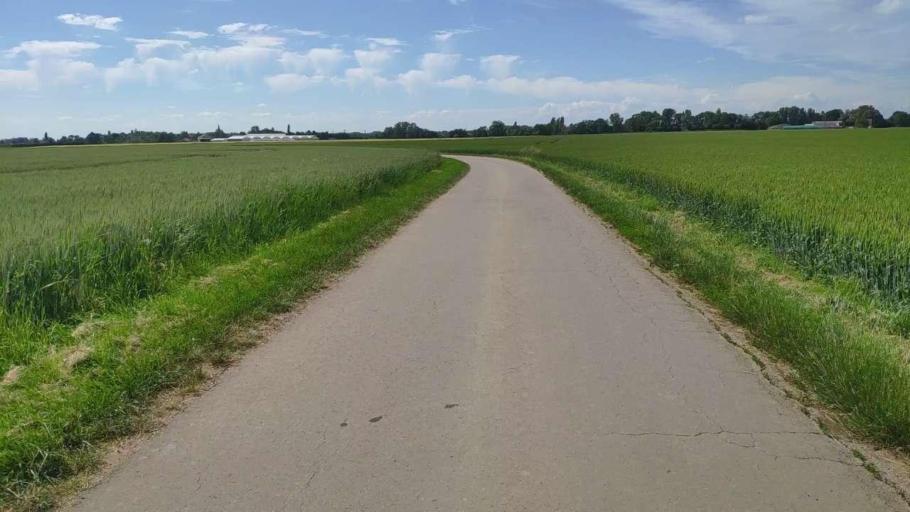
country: FR
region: Franche-Comte
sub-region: Departement du Jura
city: Bletterans
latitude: 46.7323
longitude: 5.4865
